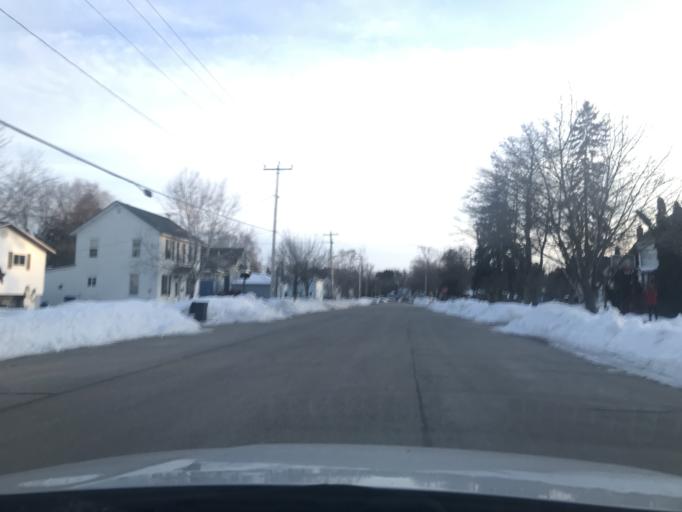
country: US
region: Wisconsin
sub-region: Marinette County
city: Peshtigo
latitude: 45.0537
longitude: -87.7419
